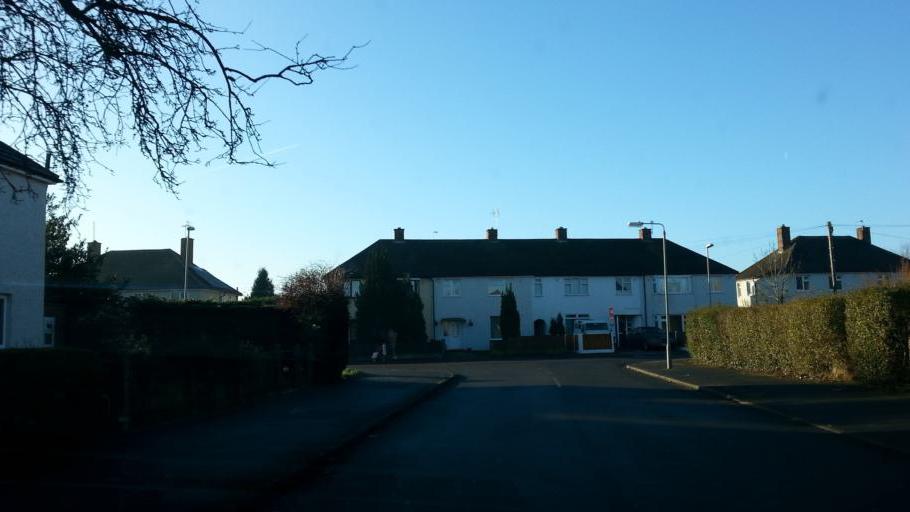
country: GB
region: England
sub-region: Nottinghamshire
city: Newark on Trent
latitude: 53.0636
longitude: -0.8178
